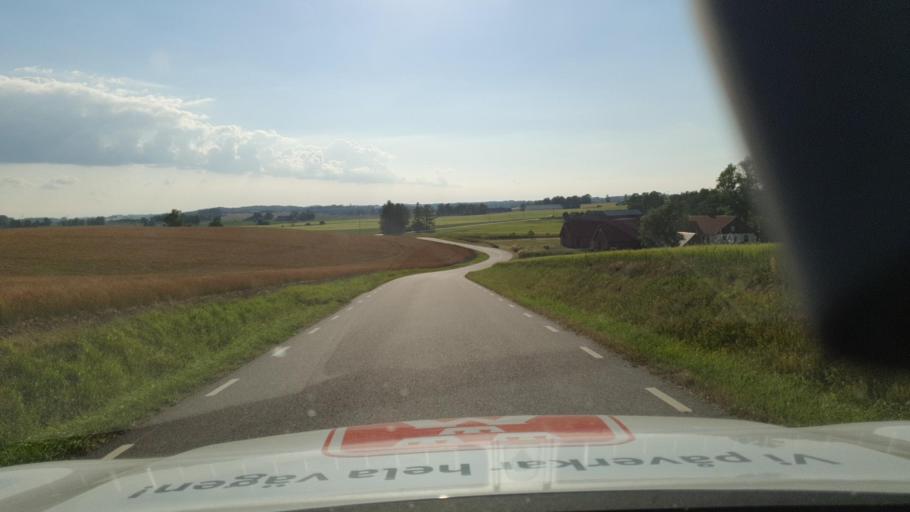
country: SE
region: Skane
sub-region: Skurups Kommun
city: Rydsgard
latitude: 55.5071
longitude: 13.5551
